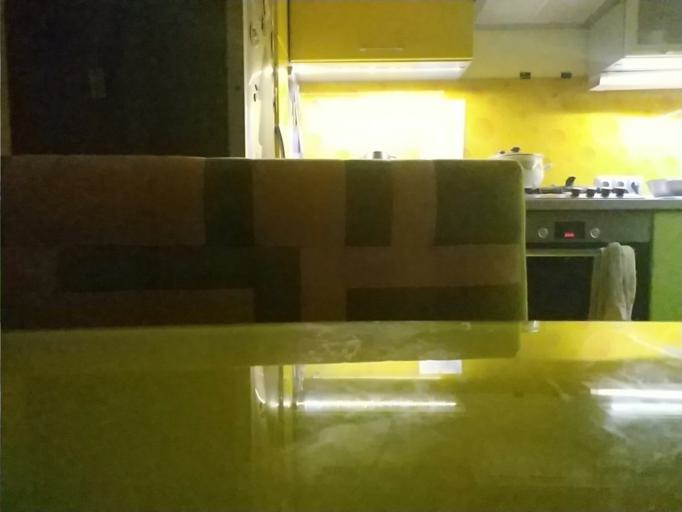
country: RU
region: Republic of Karelia
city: Pyaozerskiy
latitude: 65.7471
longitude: 30.4972
